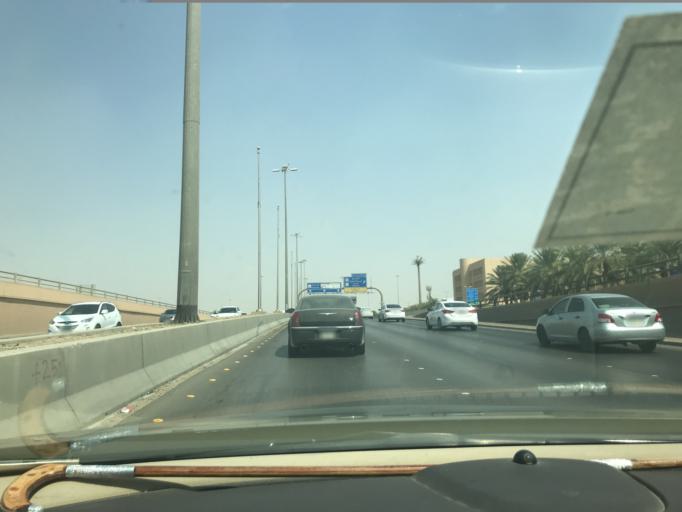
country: SA
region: Ar Riyad
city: Riyadh
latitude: 24.7110
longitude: 46.7563
